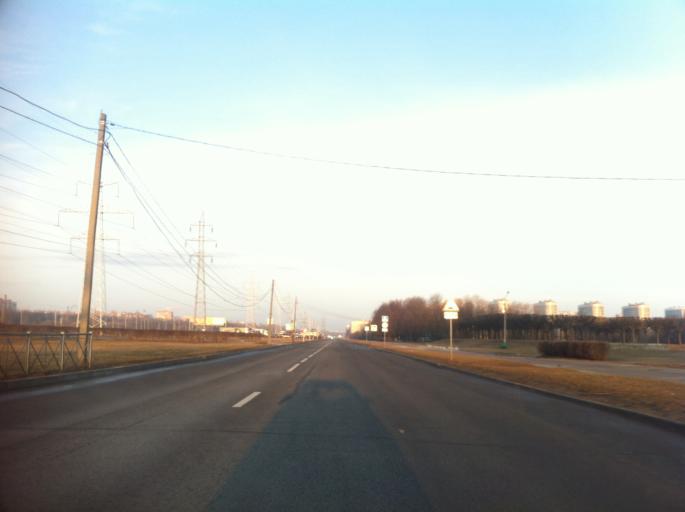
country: RU
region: St.-Petersburg
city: Uritsk
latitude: 59.8473
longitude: 30.1735
